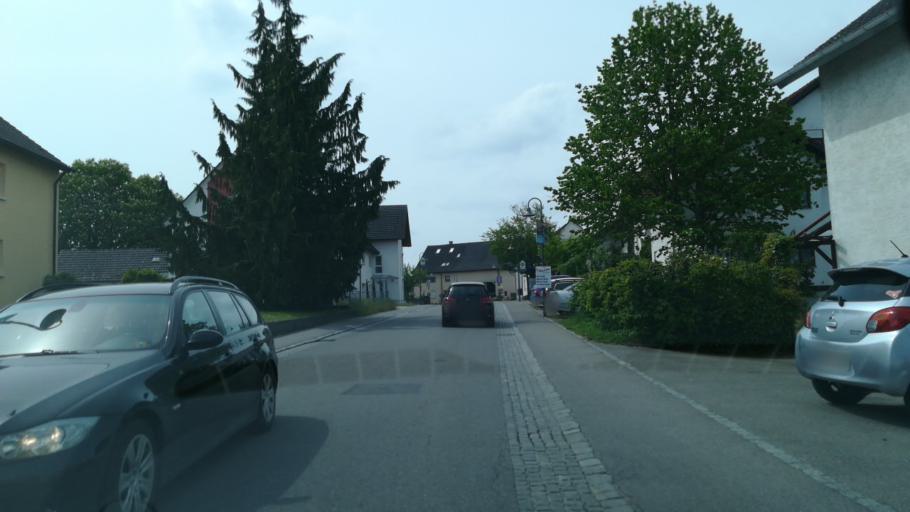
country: DE
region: Baden-Wuerttemberg
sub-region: Freiburg Region
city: Volkertshausen
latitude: 47.7898
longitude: 8.8765
